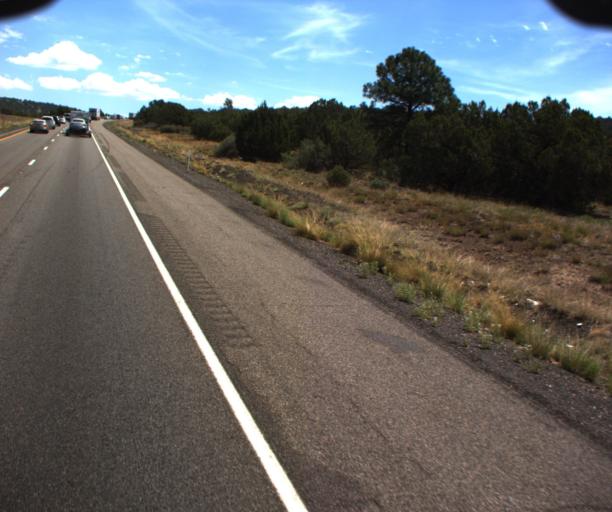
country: US
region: Arizona
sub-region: Yavapai County
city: Village of Oak Creek (Big Park)
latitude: 34.7843
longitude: -111.6066
